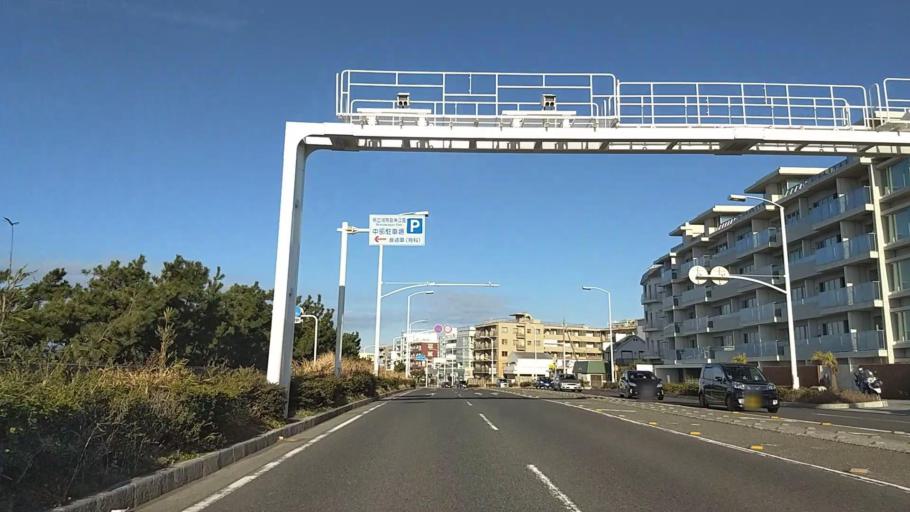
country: JP
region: Kanagawa
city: Fujisawa
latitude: 35.3126
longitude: 139.4774
